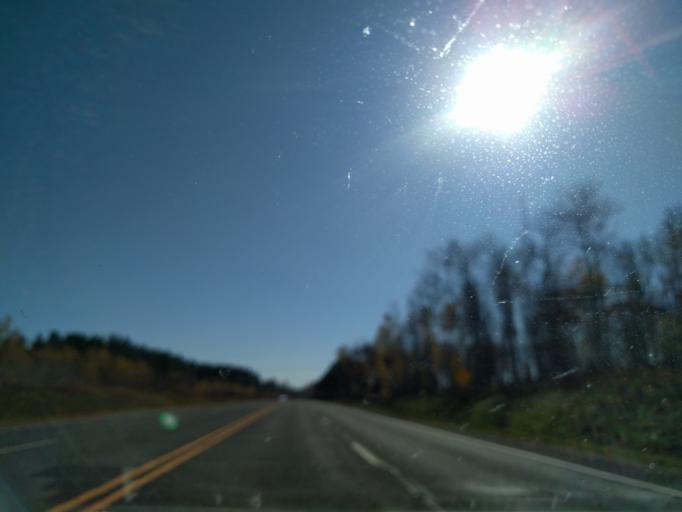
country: US
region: Michigan
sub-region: Iron County
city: Crystal Falls
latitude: 46.2264
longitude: -88.0074
